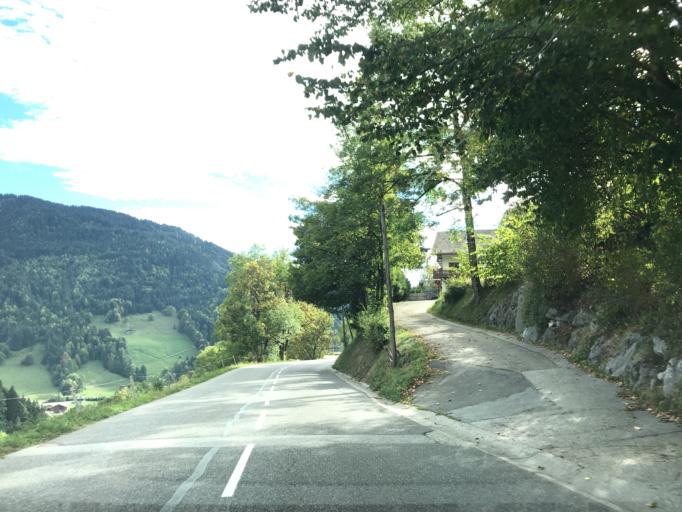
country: FR
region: Rhone-Alpes
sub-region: Departement de la Haute-Savoie
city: Le Grand-Bornand
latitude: 45.9508
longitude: 6.4362
